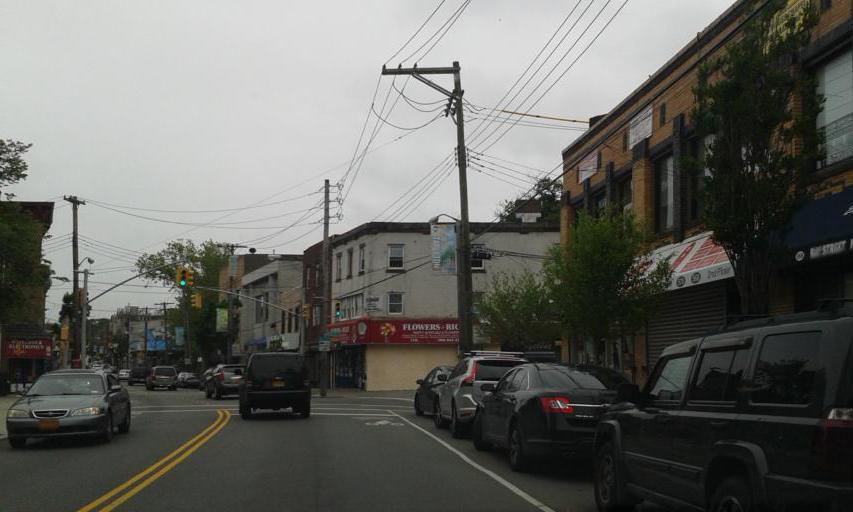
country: US
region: New Jersey
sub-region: Hudson County
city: Bayonne
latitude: 40.6283
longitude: -74.0764
